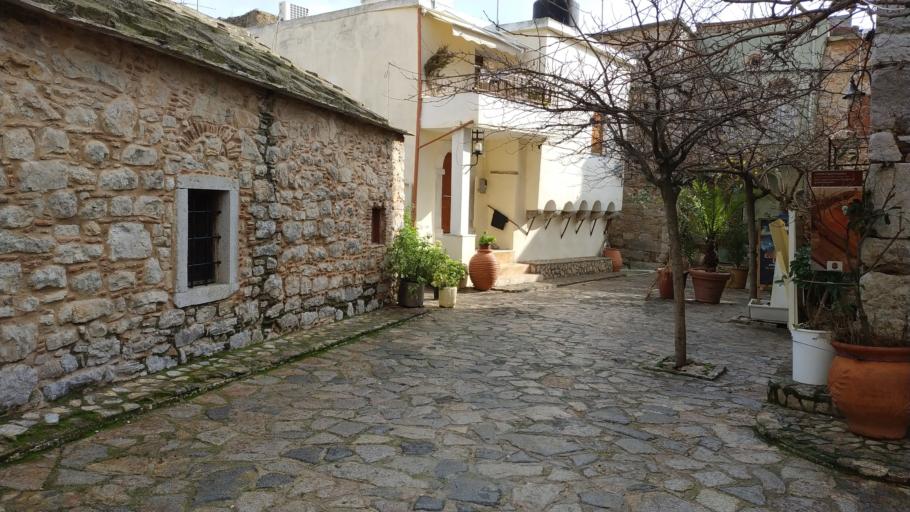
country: GR
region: North Aegean
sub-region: Chios
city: Thymiana
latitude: 38.2469
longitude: 25.9421
